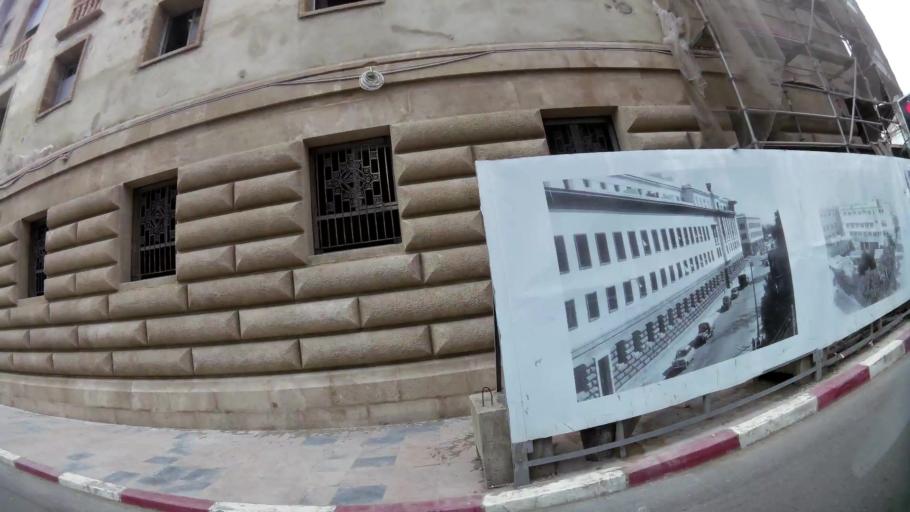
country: MA
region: Rabat-Sale-Zemmour-Zaer
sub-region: Rabat
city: Rabat
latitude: 34.0195
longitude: -6.8363
